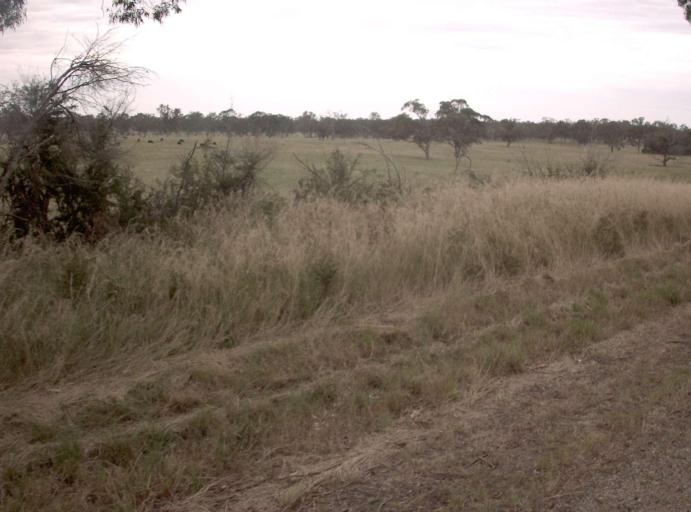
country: AU
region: Victoria
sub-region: Wellington
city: Sale
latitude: -38.1745
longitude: 147.1182
